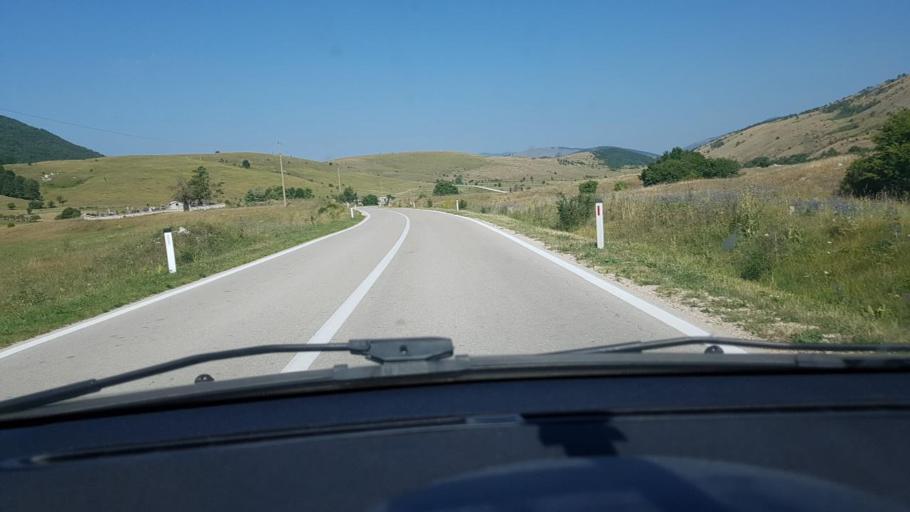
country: BA
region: Federation of Bosnia and Herzegovina
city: Bosansko Grahovo
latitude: 44.1263
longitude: 16.5201
